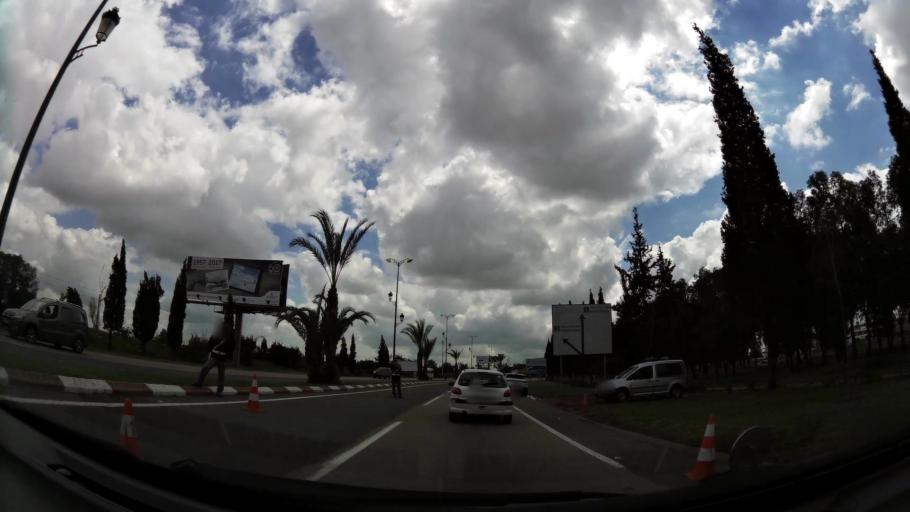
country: MA
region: Chaouia-Ouardigha
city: Nouaseur
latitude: 33.3847
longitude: -7.5648
